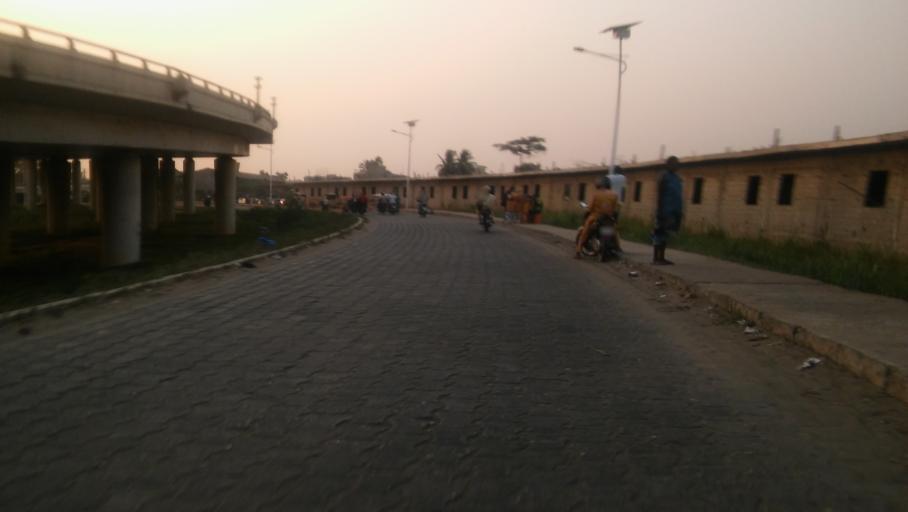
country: BJ
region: Atlantique
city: Abomey-Calavi
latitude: 6.3904
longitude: 2.3548
